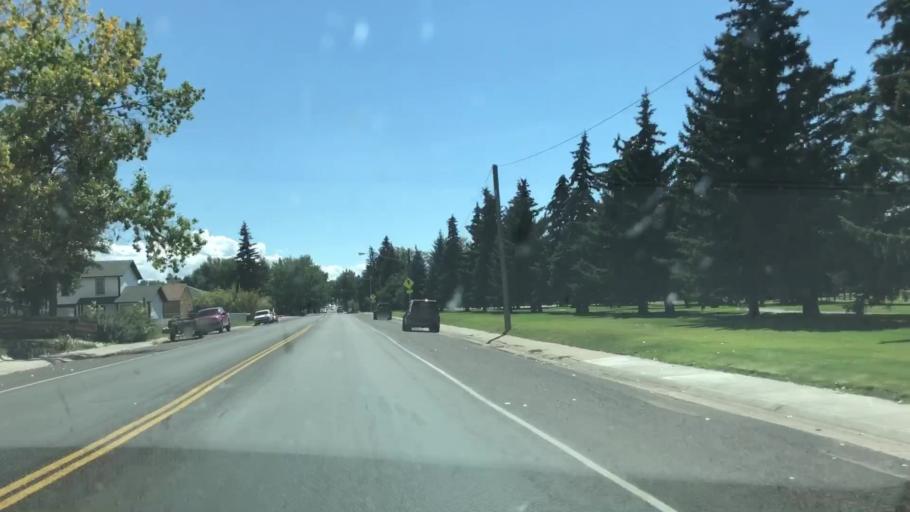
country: US
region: Wyoming
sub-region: Albany County
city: Laramie
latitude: 41.3226
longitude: -105.5845
